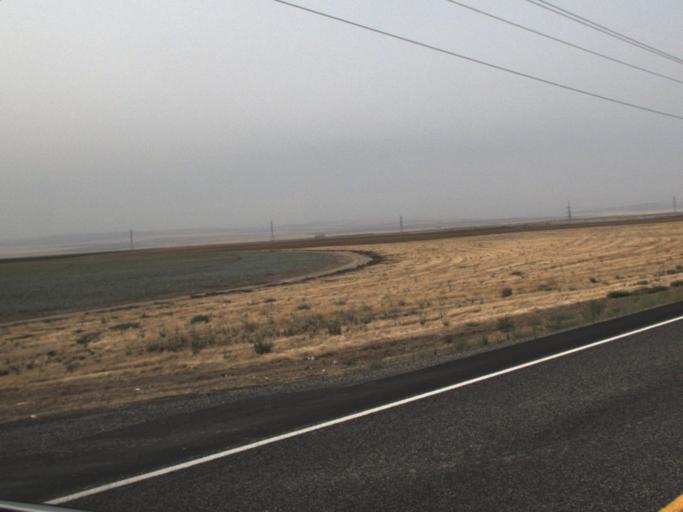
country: US
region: Oregon
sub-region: Morrow County
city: Irrigon
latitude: 46.0484
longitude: -119.6023
